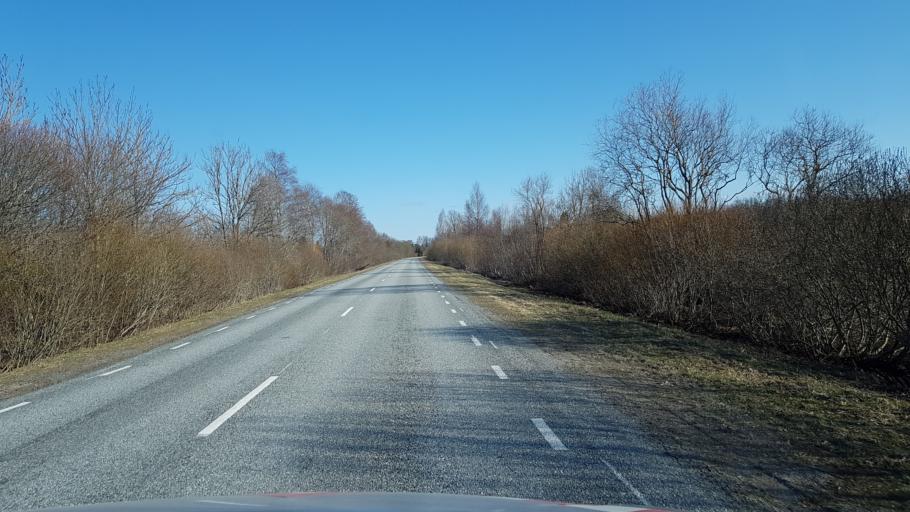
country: EE
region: Laeaene-Virumaa
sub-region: Haljala vald
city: Haljala
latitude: 59.4983
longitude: 26.1356
